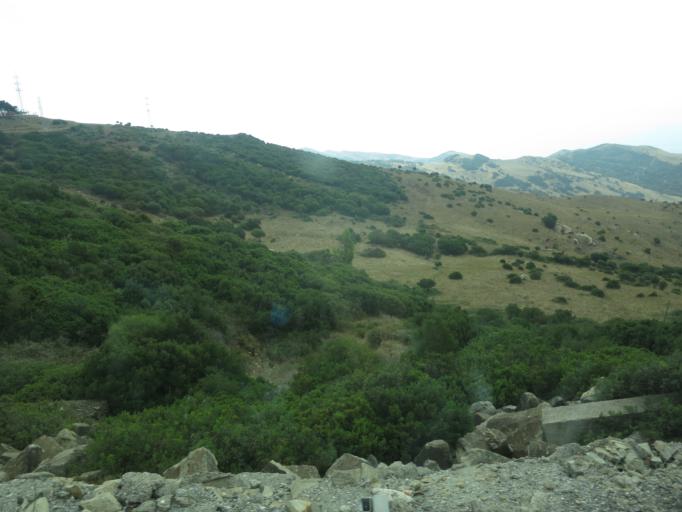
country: ES
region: Andalusia
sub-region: Provincia de Cadiz
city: Tarifa
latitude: 36.0530
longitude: -5.5539
